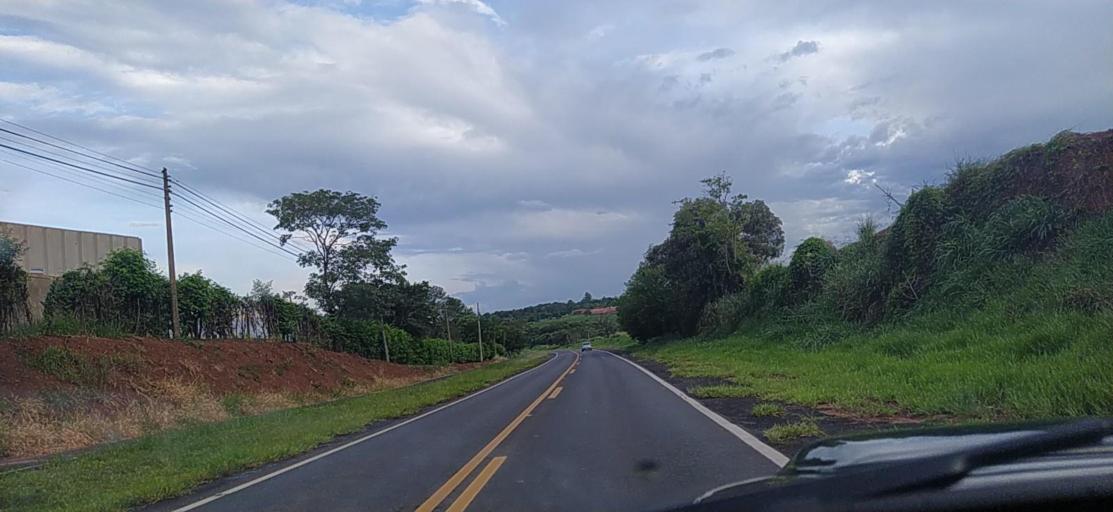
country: BR
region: Sao Paulo
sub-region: Catanduva
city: Catanduva
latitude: -21.1571
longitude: -48.9512
